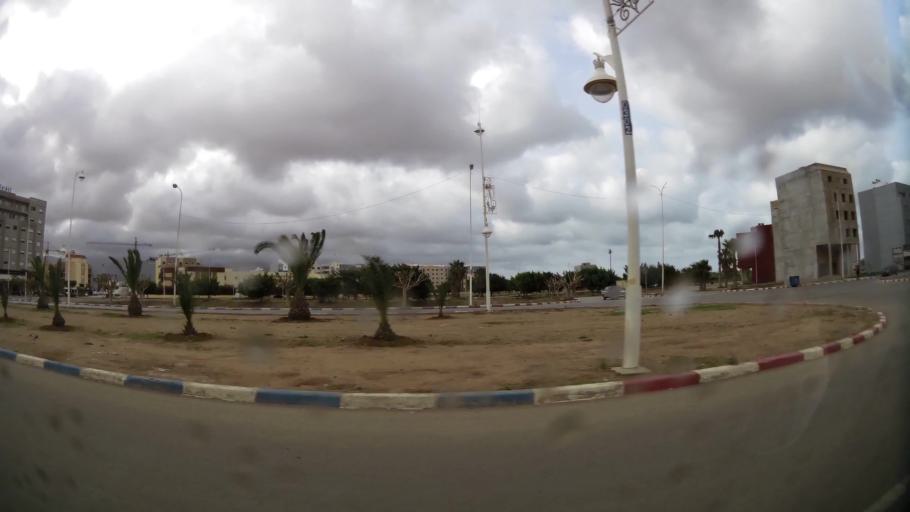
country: MA
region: Oriental
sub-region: Nador
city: Nador
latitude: 35.1526
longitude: -2.9217
